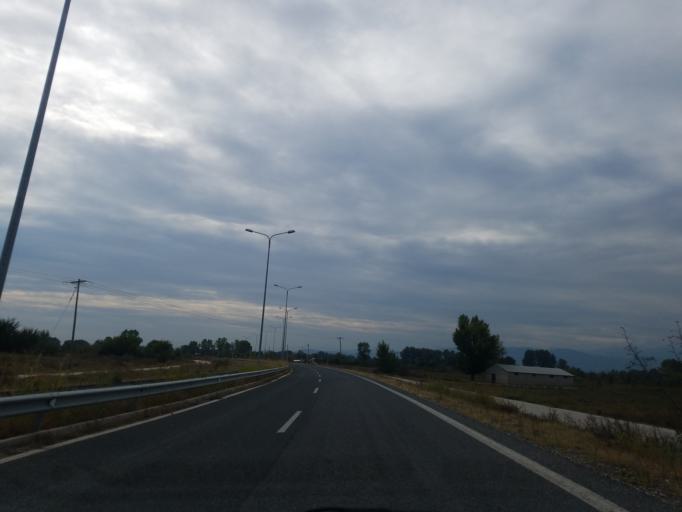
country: GR
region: Thessaly
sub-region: Trikala
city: Pyrgetos
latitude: 39.5383
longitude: 21.7361
